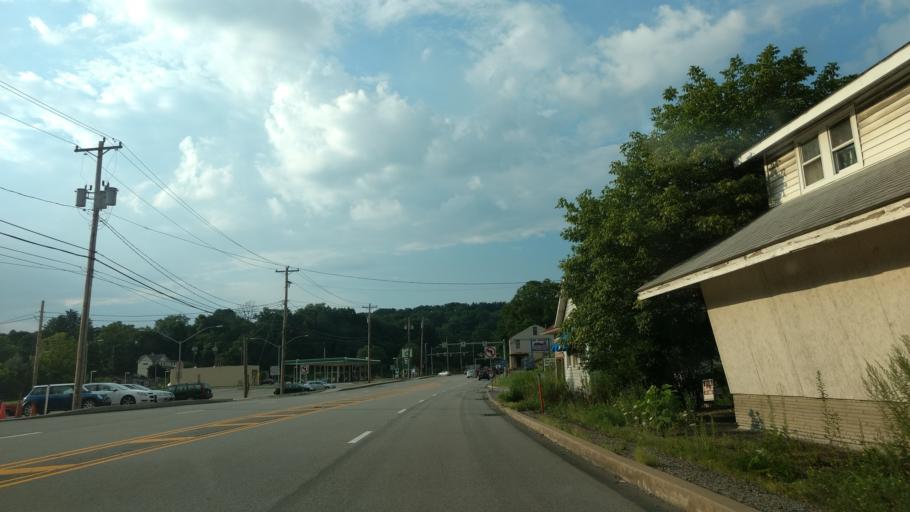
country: US
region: Pennsylvania
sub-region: Allegheny County
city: Allison Park
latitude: 40.5576
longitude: -79.9589
